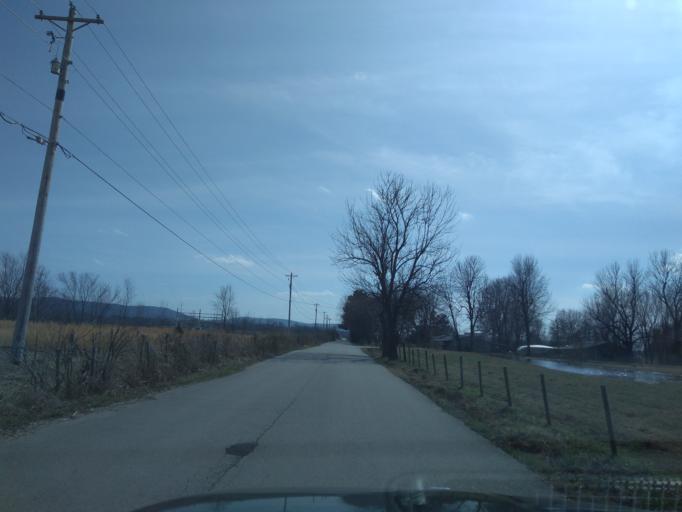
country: US
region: Arkansas
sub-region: Washington County
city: Farmington
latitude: 36.0687
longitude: -94.2399
